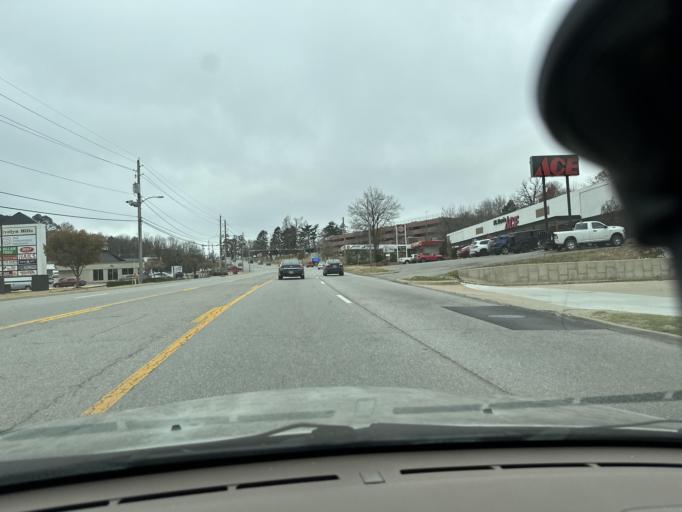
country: US
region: Arkansas
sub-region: Washington County
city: Fayetteville
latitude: 36.0827
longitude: -94.1561
